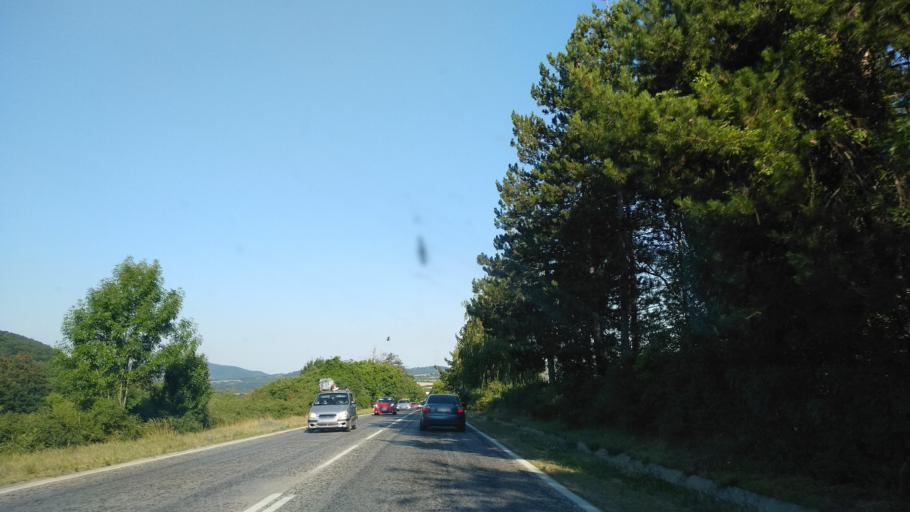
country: BG
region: Gabrovo
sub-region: Obshtina Sevlievo
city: Sevlievo
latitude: 43.0492
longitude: 24.9187
